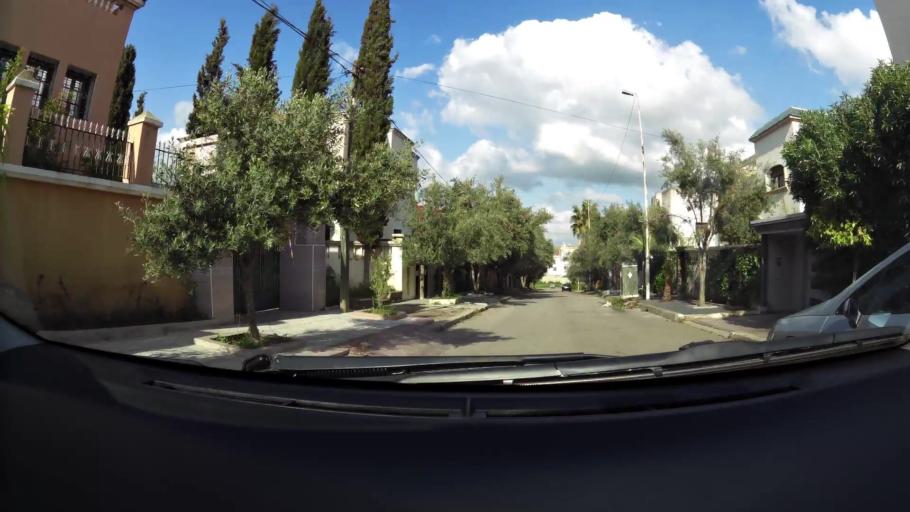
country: MA
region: Chaouia-Ouardigha
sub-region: Settat Province
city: Settat
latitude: 33.0105
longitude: -7.6289
